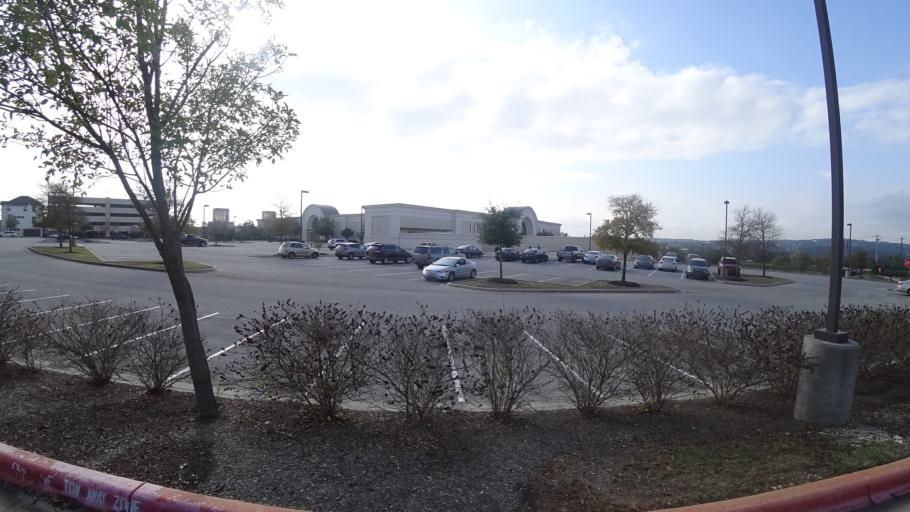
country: US
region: Texas
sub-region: Travis County
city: Bee Cave
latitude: 30.3115
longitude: -97.9444
